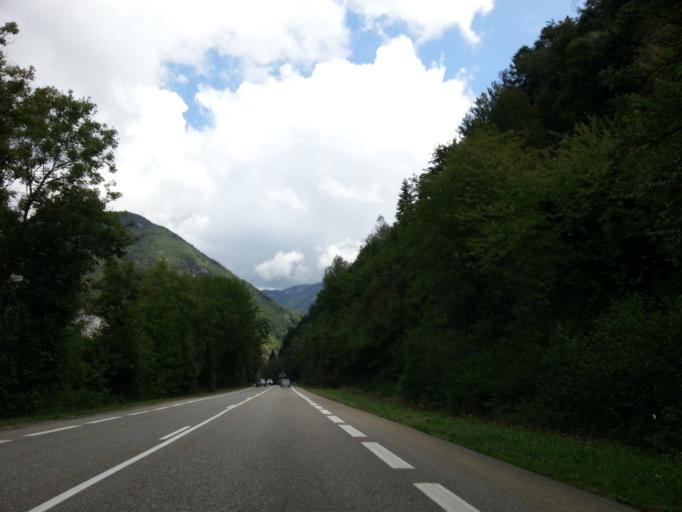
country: FR
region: Rhone-Alpes
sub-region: Departement de la Haute-Savoie
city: Thones
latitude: 45.8965
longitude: 6.2766
